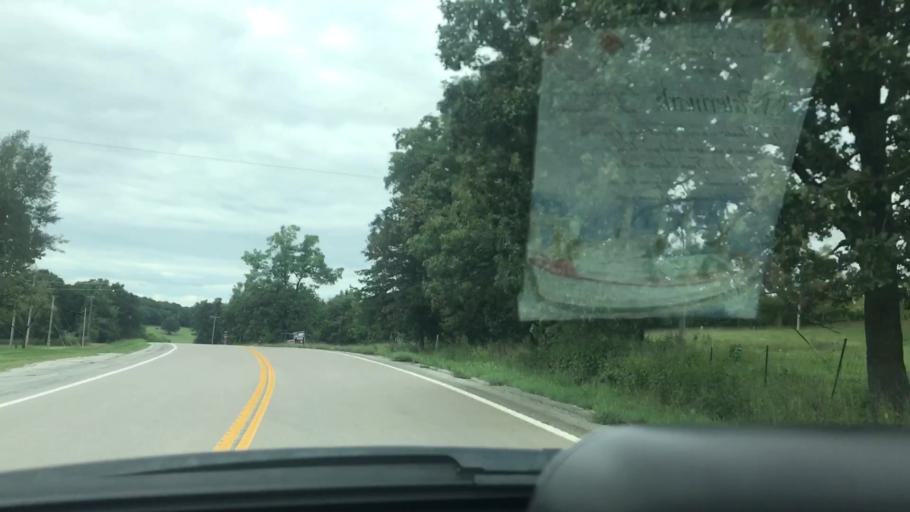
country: US
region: Missouri
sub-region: Benton County
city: Warsaw
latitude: 38.1194
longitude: -93.2761
